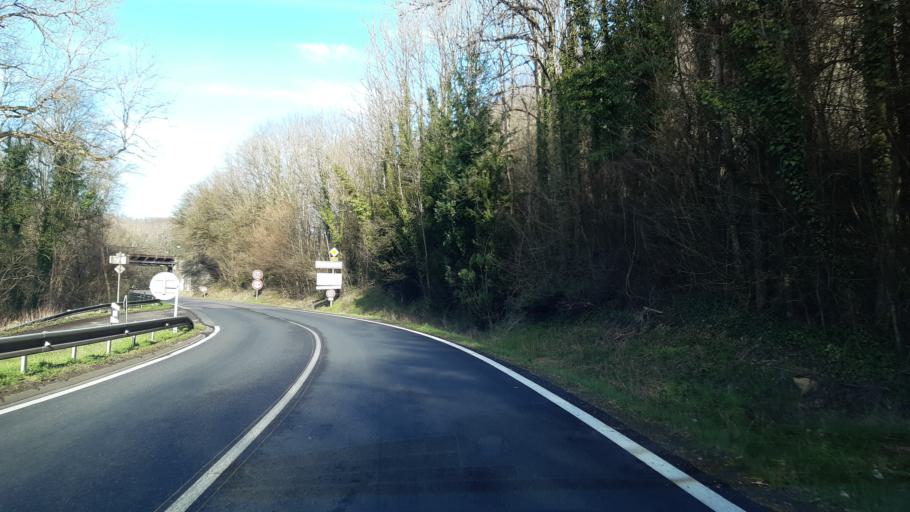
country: FR
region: Lorraine
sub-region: Departement de la Moselle
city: Audun-le-Tiche
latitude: 49.4640
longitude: 5.9636
